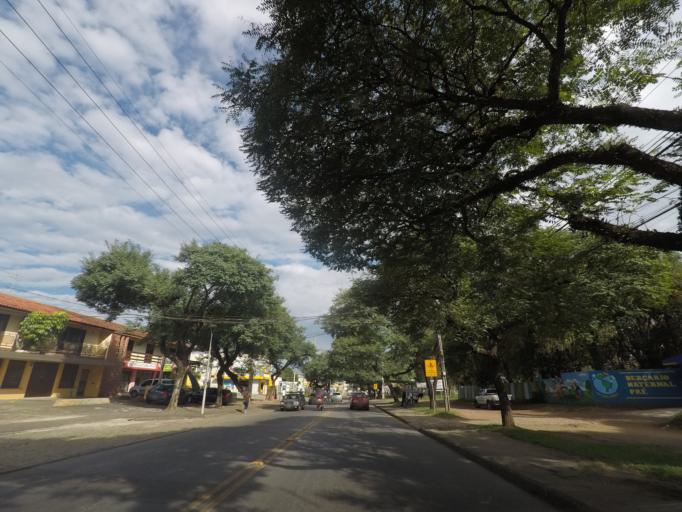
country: BR
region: Parana
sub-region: Sao Jose Dos Pinhais
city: Sao Jose dos Pinhais
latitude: -25.5373
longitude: -49.2950
